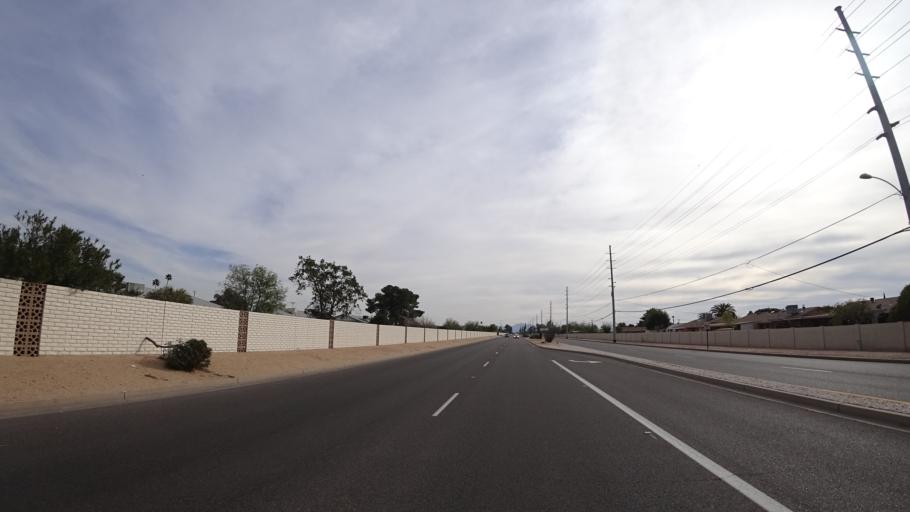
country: US
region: Arizona
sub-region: Maricopa County
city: Sun City
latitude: 33.5929
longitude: -112.2726
